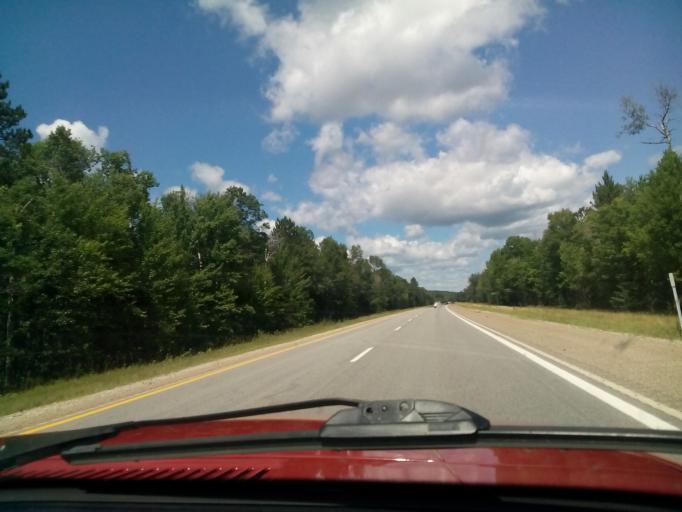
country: US
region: Michigan
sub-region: Roscommon County
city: Roscommon
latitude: 44.4289
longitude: -84.5986
